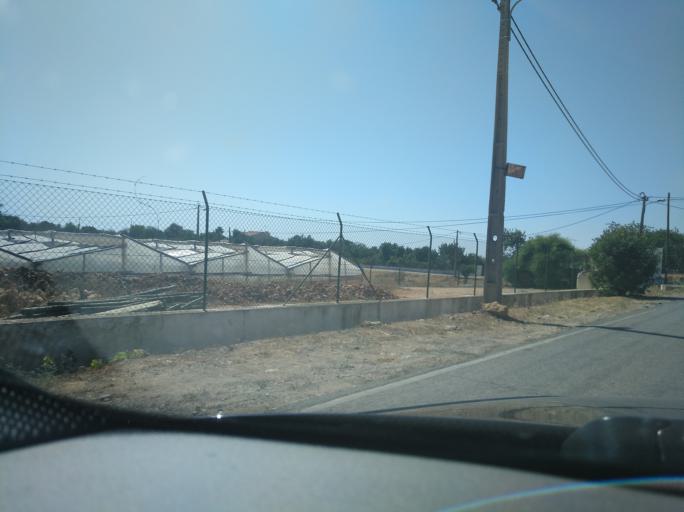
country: PT
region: Faro
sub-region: Faro
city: Faro
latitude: 37.0540
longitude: -7.9014
